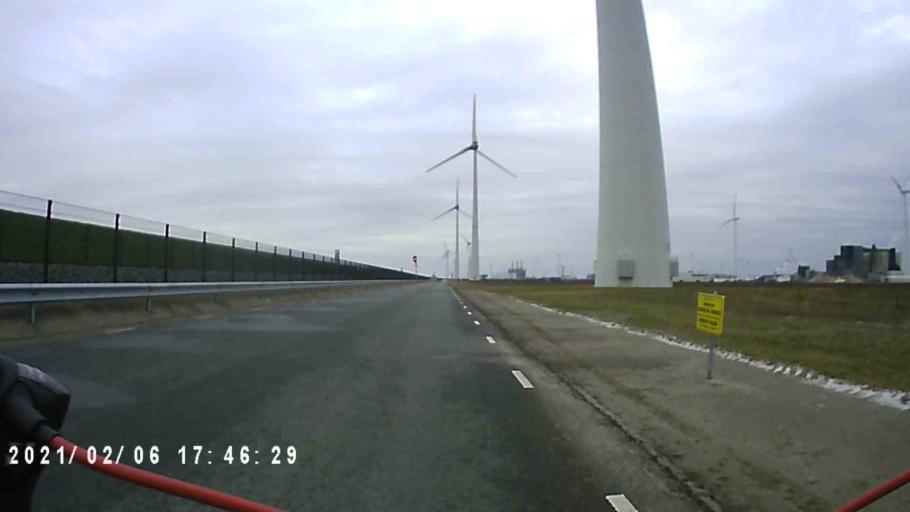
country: NL
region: Groningen
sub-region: Gemeente Appingedam
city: Appingedam
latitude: 53.4607
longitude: 6.8220
